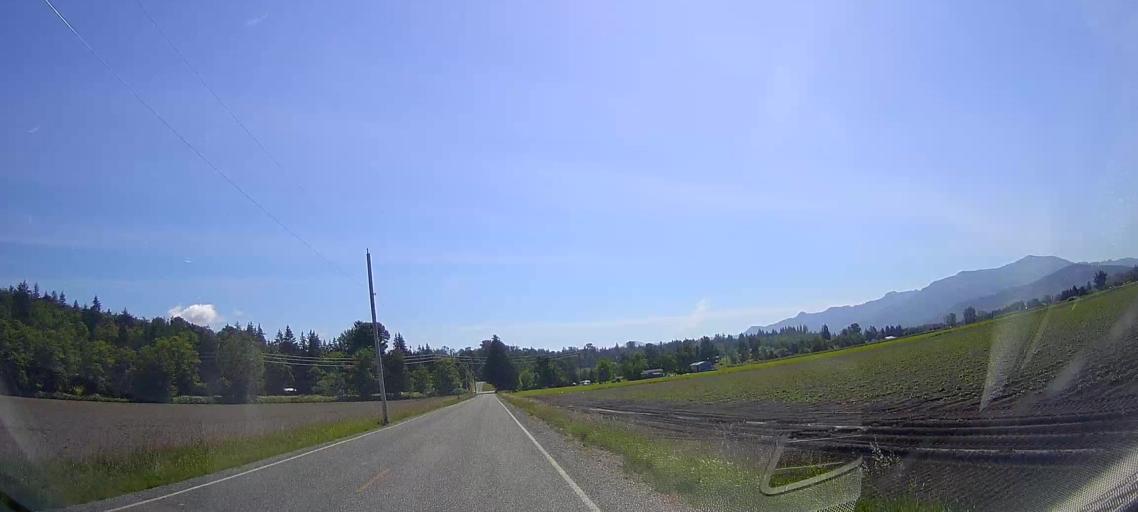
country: US
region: Washington
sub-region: Skagit County
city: Sedro-Woolley
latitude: 48.5288
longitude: -122.2829
